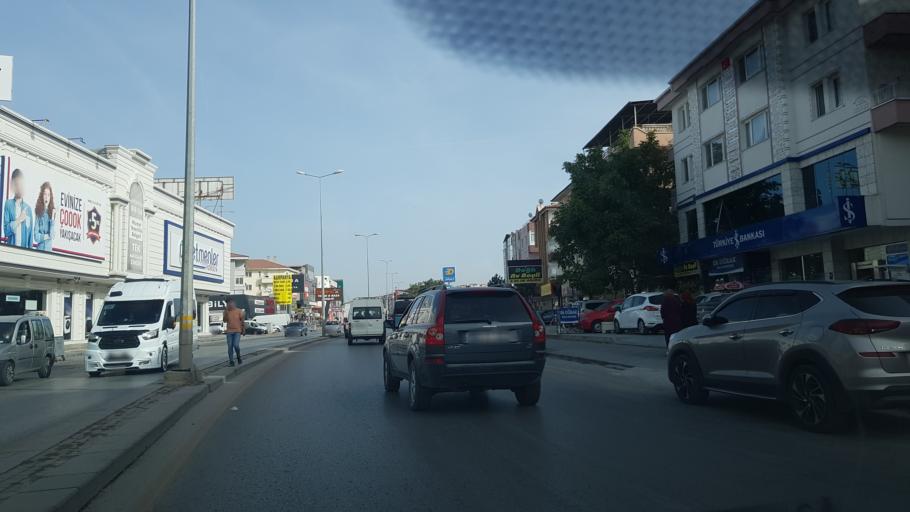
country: TR
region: Ankara
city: Etimesgut
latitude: 39.9542
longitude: 32.6344
